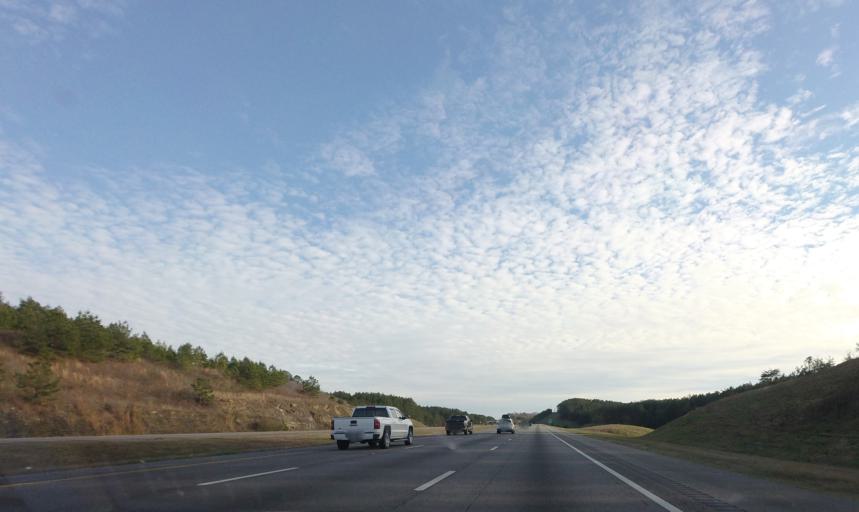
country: US
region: Alabama
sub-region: Walker County
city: Cordova
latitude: 33.7302
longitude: -87.1933
